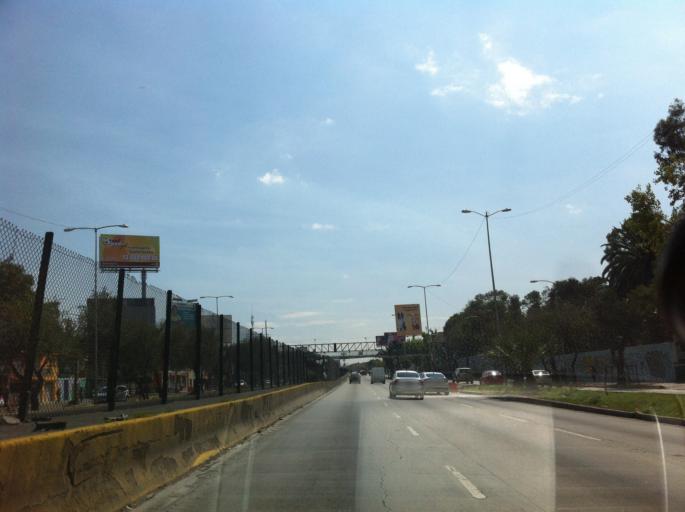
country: MX
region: Mexico City
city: Cuauhtemoc
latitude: 19.4644
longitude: -99.1325
